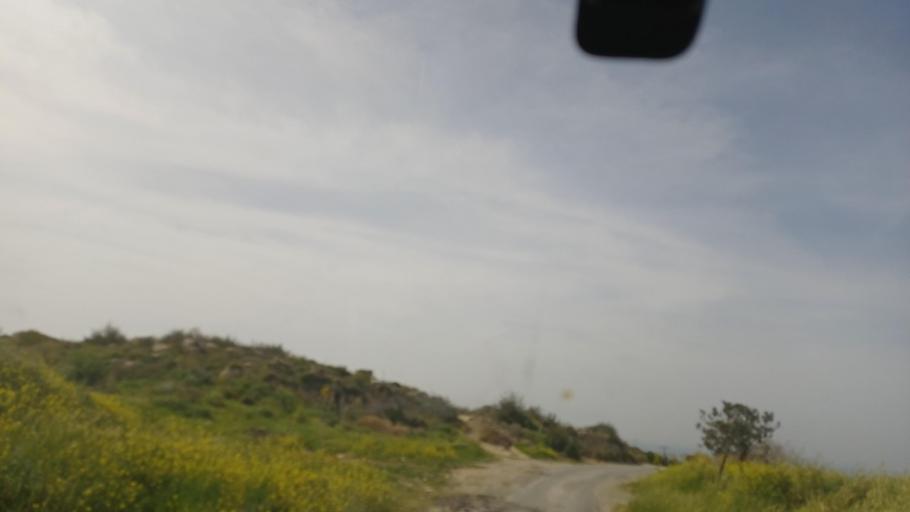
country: CY
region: Pafos
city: Mesogi
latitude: 34.7746
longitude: 32.4821
